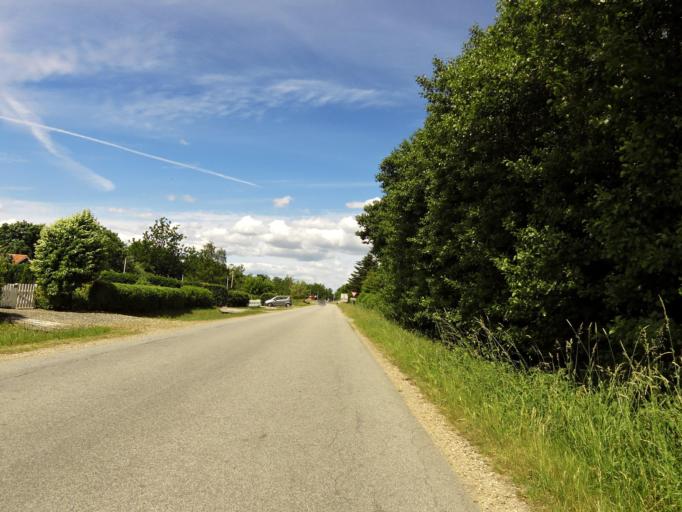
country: DK
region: South Denmark
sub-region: Esbjerg Kommune
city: Ribe
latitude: 55.3182
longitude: 8.7611
